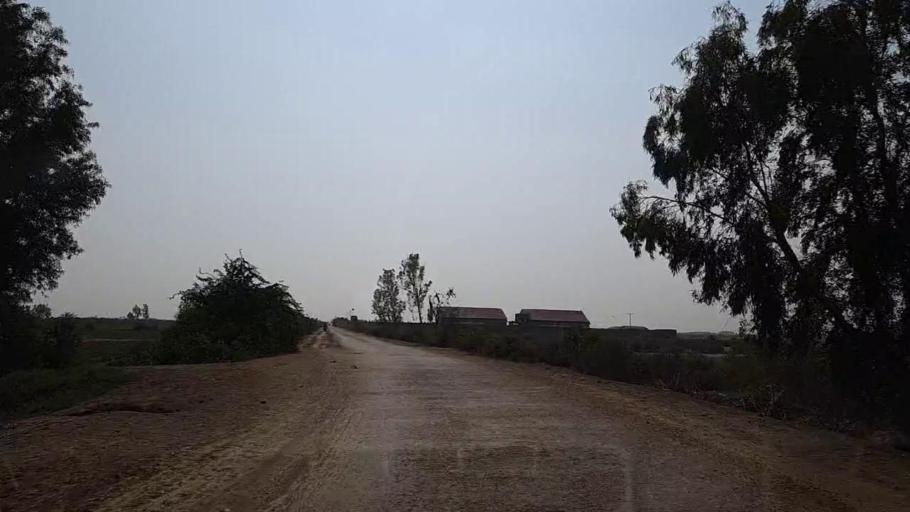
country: PK
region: Sindh
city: Thatta
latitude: 24.7103
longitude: 67.7674
